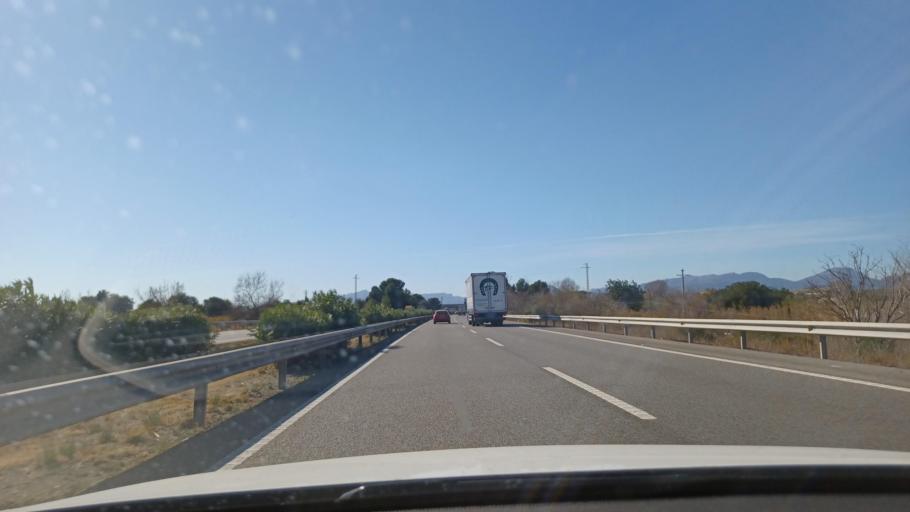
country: ES
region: Catalonia
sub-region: Provincia de Tarragona
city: Cambrils
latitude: 41.0853
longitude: 1.0747
